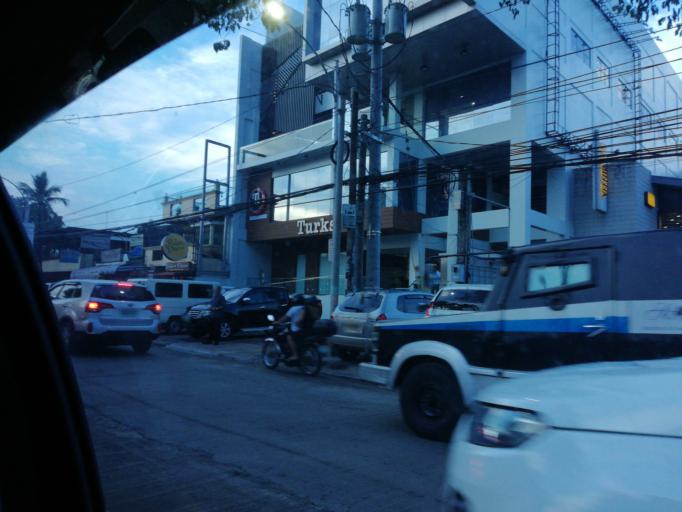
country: PH
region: Metro Manila
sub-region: Quezon City
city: Quezon City
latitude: 14.6585
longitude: 121.0451
